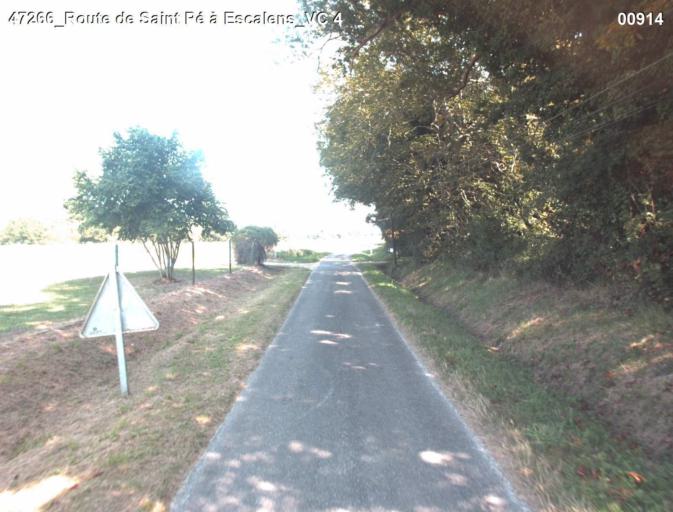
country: FR
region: Aquitaine
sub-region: Departement des Landes
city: Gabarret
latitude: 44.0019
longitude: 0.0715
